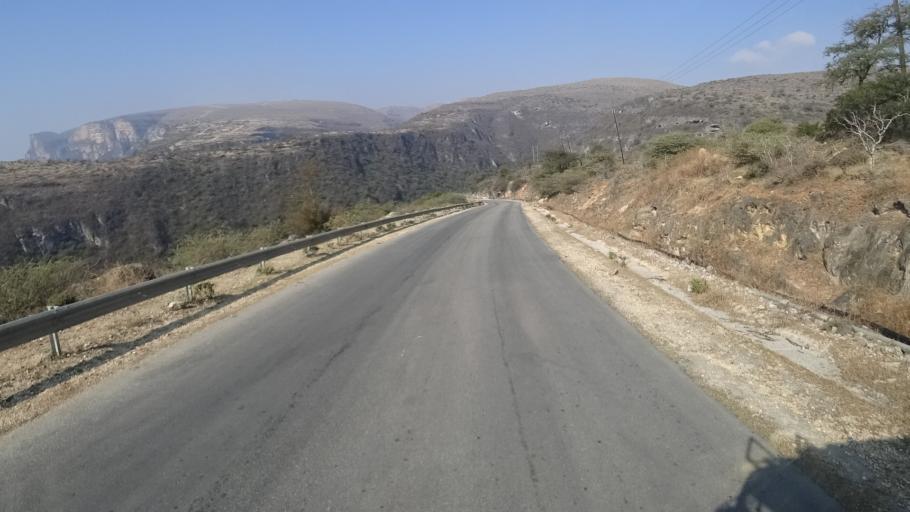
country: YE
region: Al Mahrah
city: Hawf
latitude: 16.7091
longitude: 53.1468
